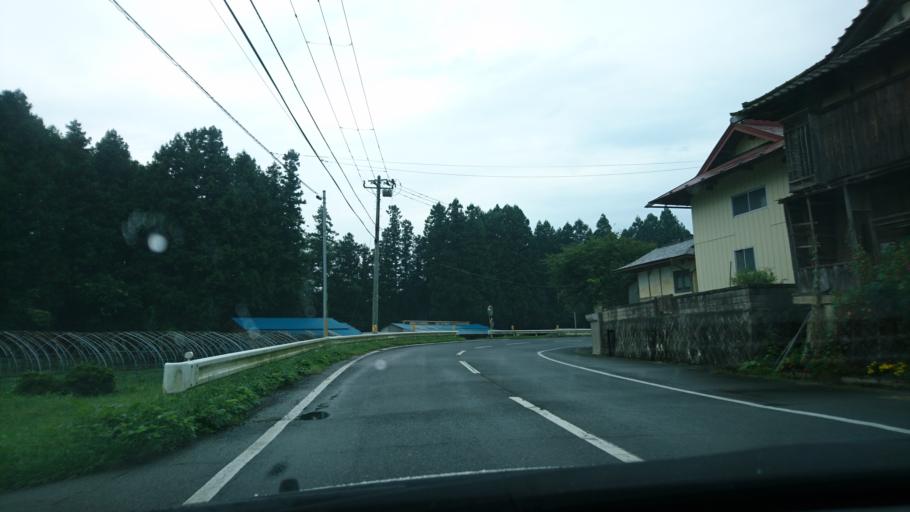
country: JP
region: Iwate
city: Ichinoseki
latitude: 38.8797
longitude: 141.2631
